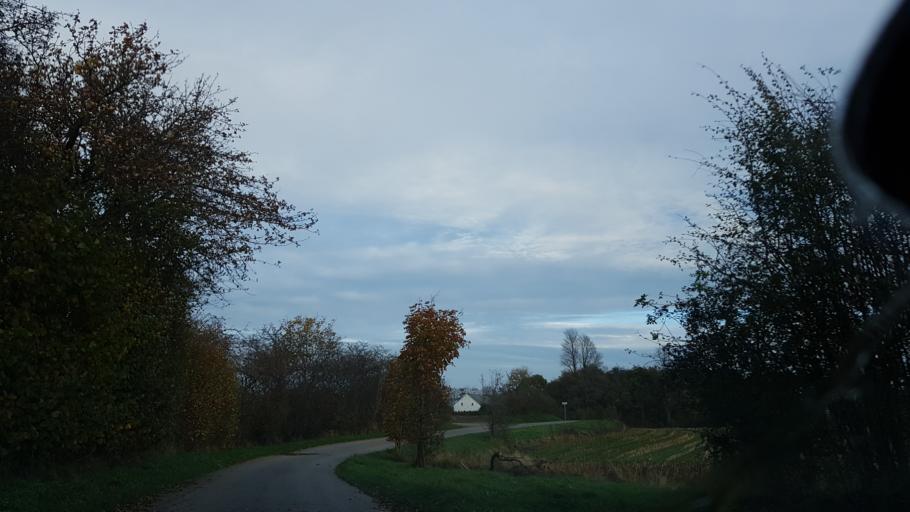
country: DK
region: South Denmark
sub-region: Haderslev Kommune
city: Vojens
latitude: 55.3210
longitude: 9.3658
